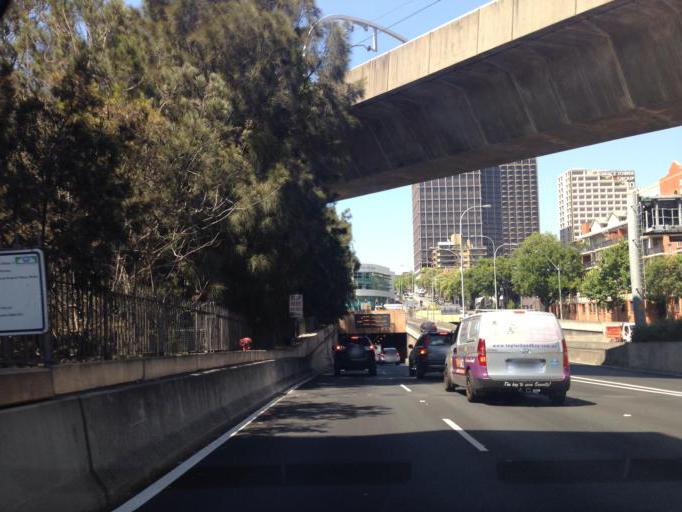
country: AU
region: New South Wales
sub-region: City of Sydney
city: Darlinghurst
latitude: -33.8710
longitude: 151.2183
